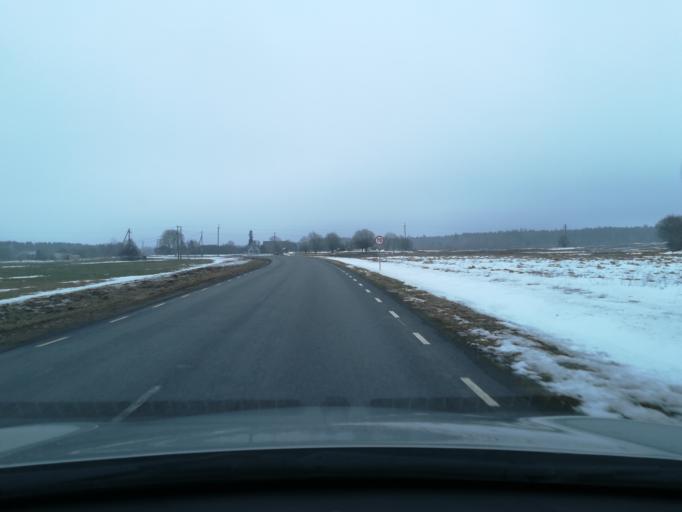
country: EE
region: Harju
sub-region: Kuusalu vald
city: Kuusalu
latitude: 59.4721
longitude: 25.5544
